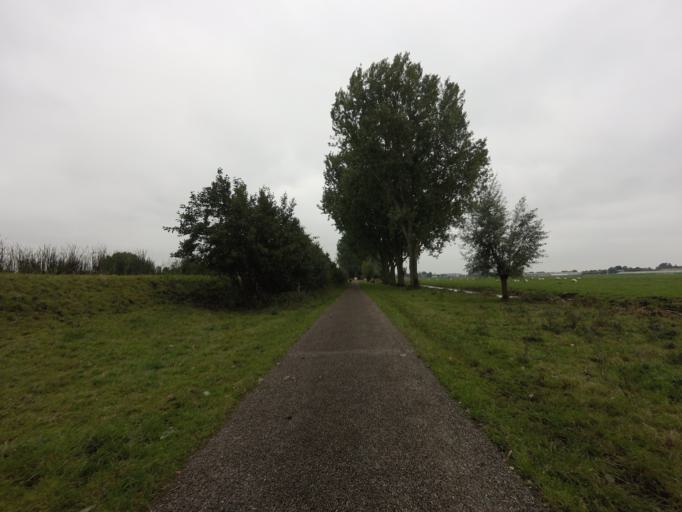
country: NL
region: North Holland
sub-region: Gemeente Aalsmeer
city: Aalsmeer
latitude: 52.2010
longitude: 4.7363
